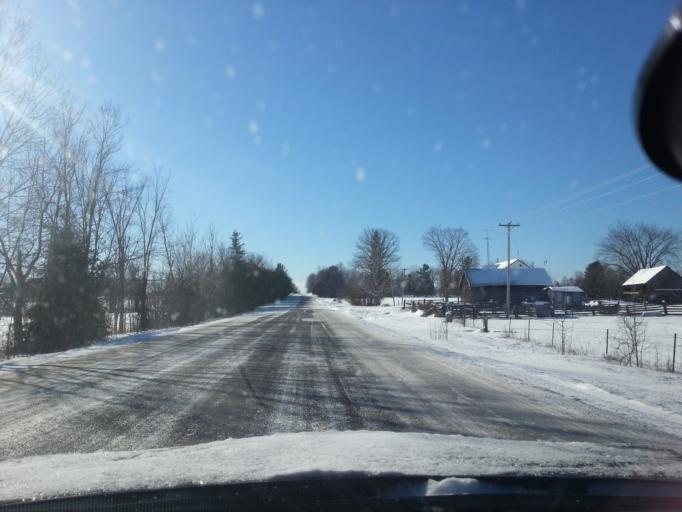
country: CA
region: Ontario
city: Arnprior
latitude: 45.2872
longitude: -76.2928
